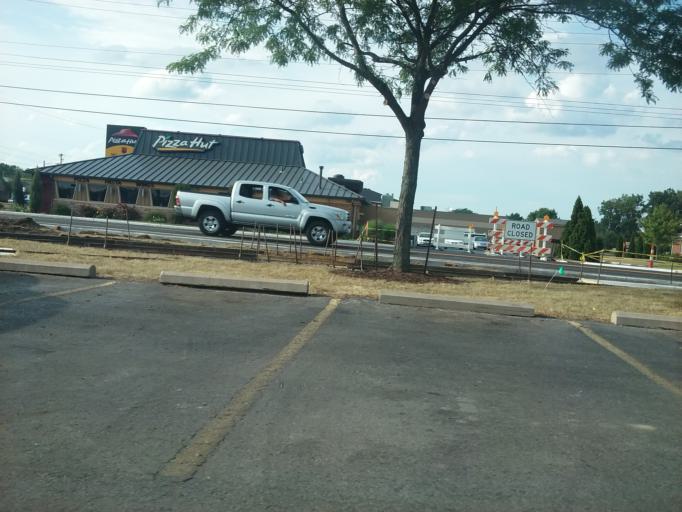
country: US
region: Ohio
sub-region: Wood County
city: Bowling Green
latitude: 41.3564
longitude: -83.6495
